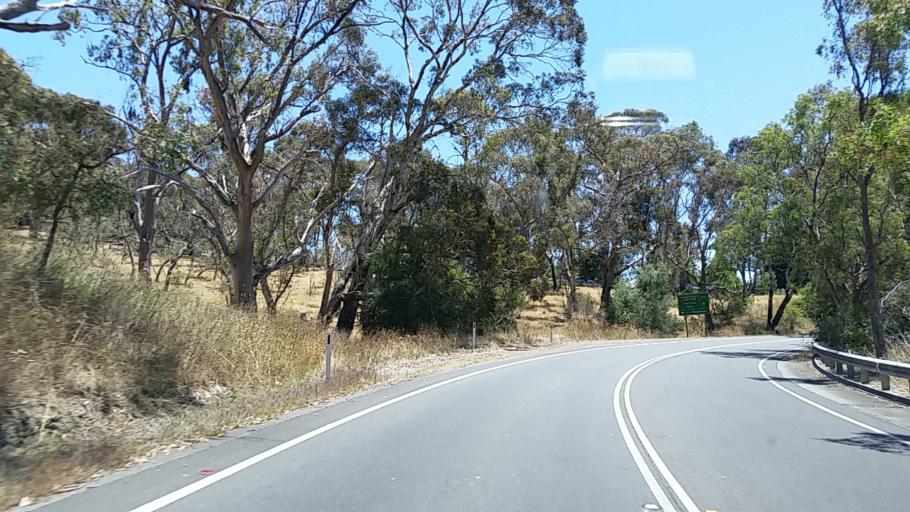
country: AU
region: South Australia
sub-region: Tea Tree Gully
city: Golden Grove
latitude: -34.8254
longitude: 138.7662
